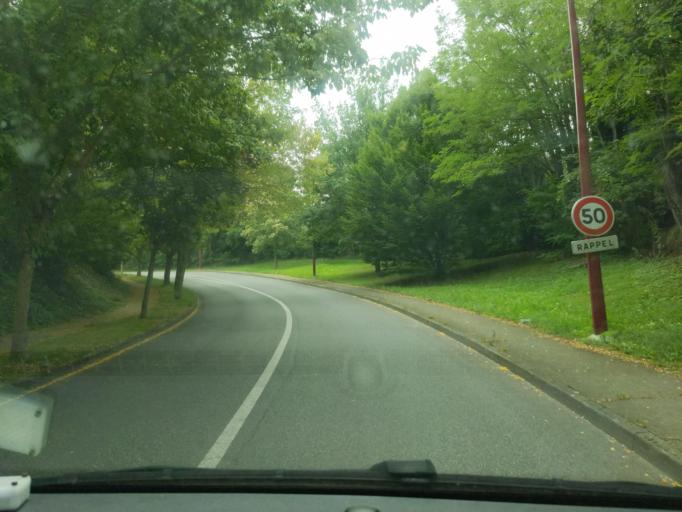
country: FR
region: Midi-Pyrenees
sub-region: Departement de la Haute-Garonne
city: Ramonville-Saint-Agne
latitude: 43.5366
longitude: 1.4769
